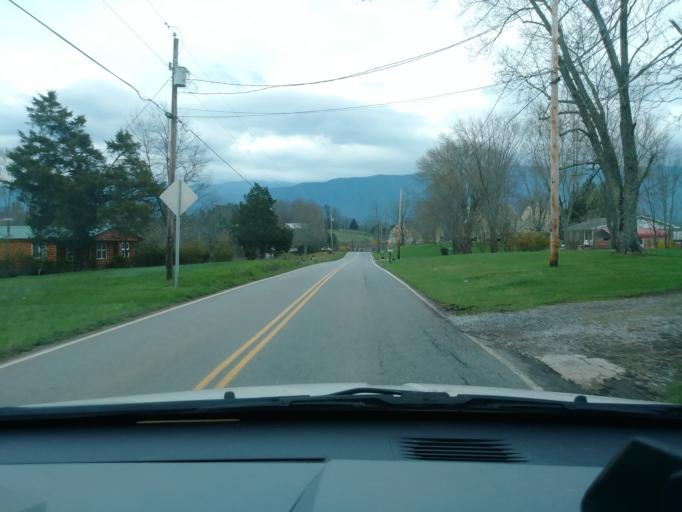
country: US
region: Tennessee
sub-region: Greene County
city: Tusculum
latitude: 36.0968
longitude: -82.7626
